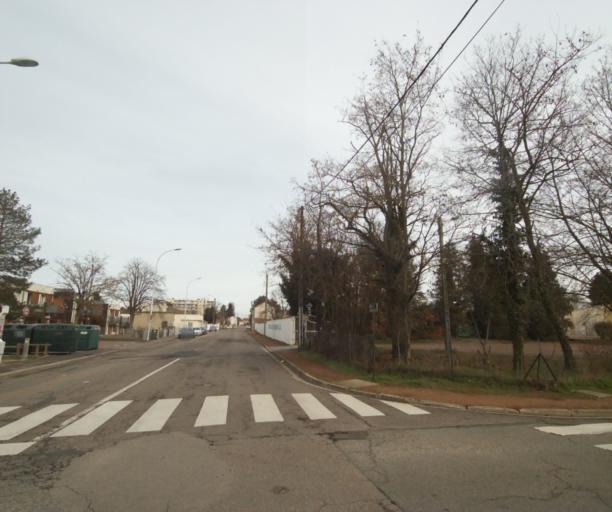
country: FR
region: Rhone-Alpes
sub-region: Departement de la Loire
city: Roanne
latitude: 46.0203
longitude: 4.0552
